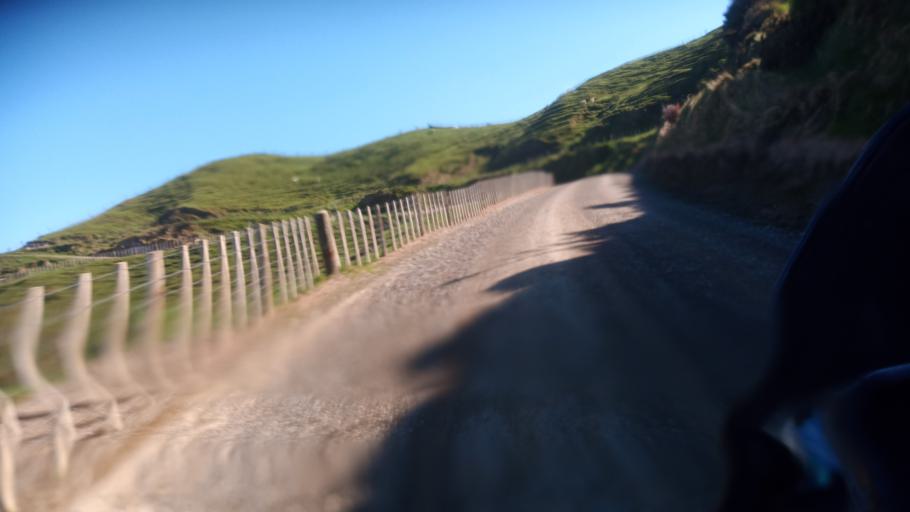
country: NZ
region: Gisborne
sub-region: Gisborne District
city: Gisborne
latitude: -39.1664
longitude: 177.8982
